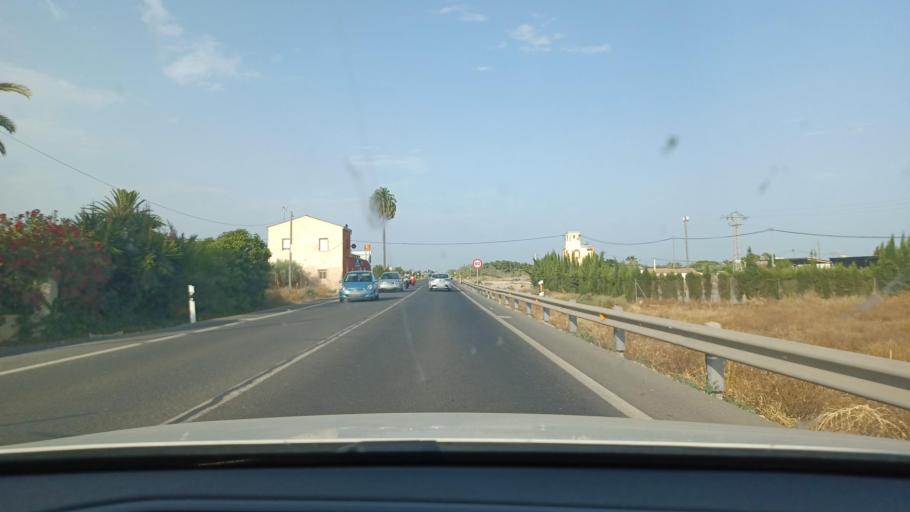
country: ES
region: Valencia
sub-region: Provincia de Alicante
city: Elche
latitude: 38.2788
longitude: -0.6458
